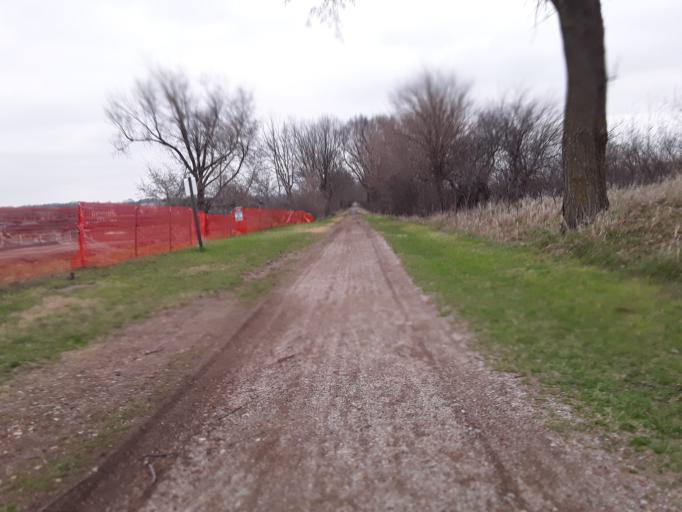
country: US
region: Nebraska
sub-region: Lancaster County
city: Lincoln
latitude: 40.8513
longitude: -96.5990
